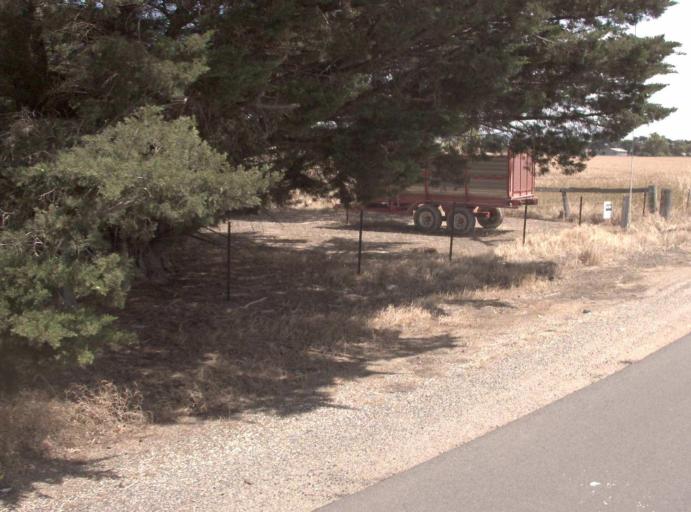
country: AU
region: Victoria
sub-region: Wellington
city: Heyfield
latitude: -38.1194
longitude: 146.8603
